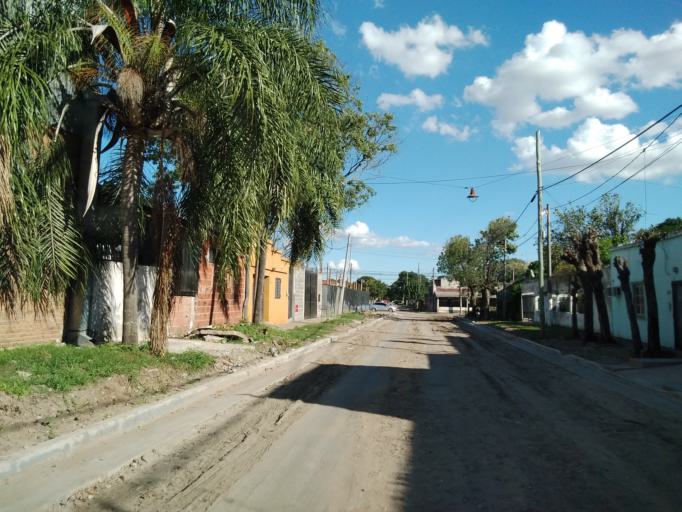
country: AR
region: Corrientes
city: Corrientes
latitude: -27.4757
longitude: -58.8510
